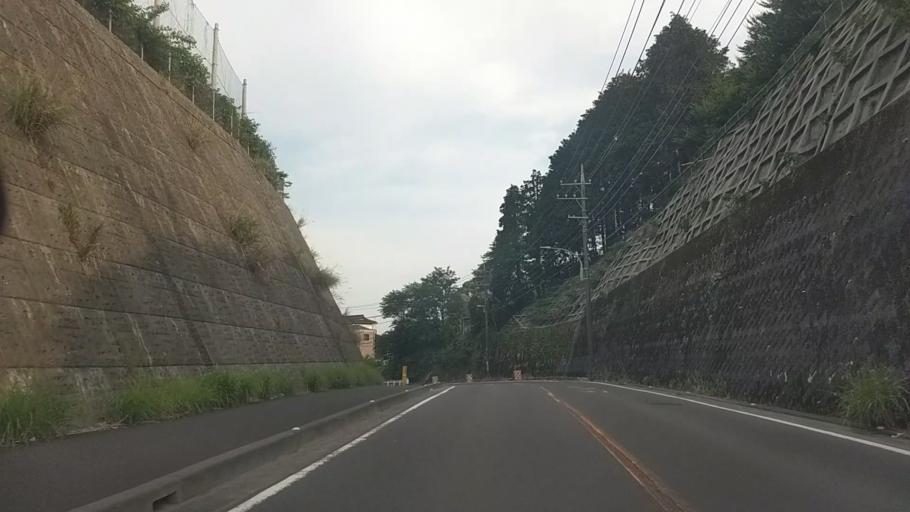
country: JP
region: Kanagawa
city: Odawara
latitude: 35.3577
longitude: 139.0889
